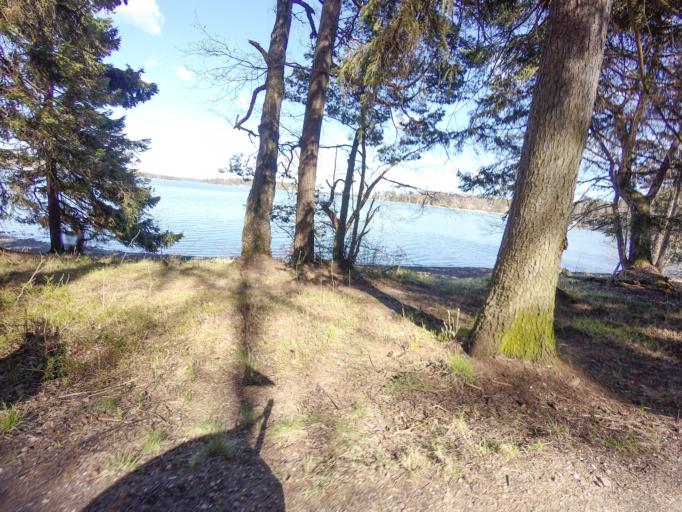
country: FI
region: Uusimaa
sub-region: Helsinki
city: Vantaa
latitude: 60.1706
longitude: 25.0666
